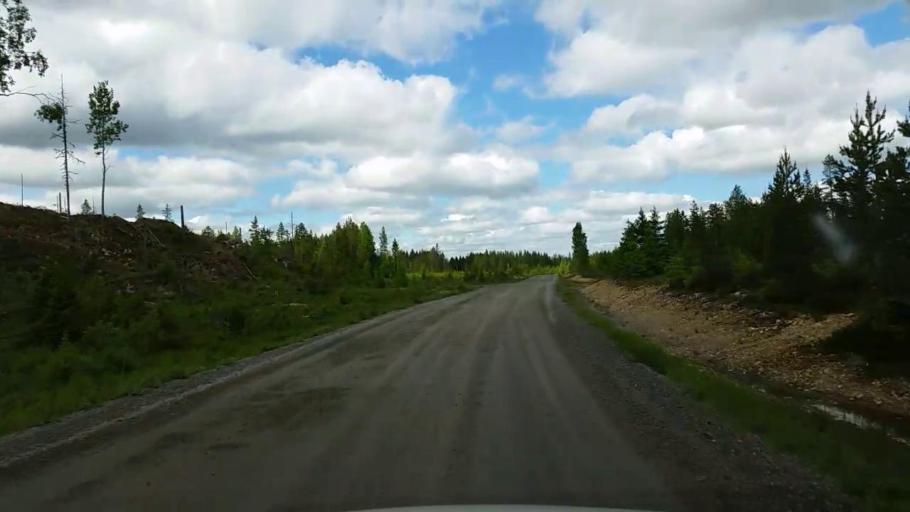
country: SE
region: Gaevleborg
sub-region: Bollnas Kommun
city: Vittsjo
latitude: 61.1708
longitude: 16.1542
